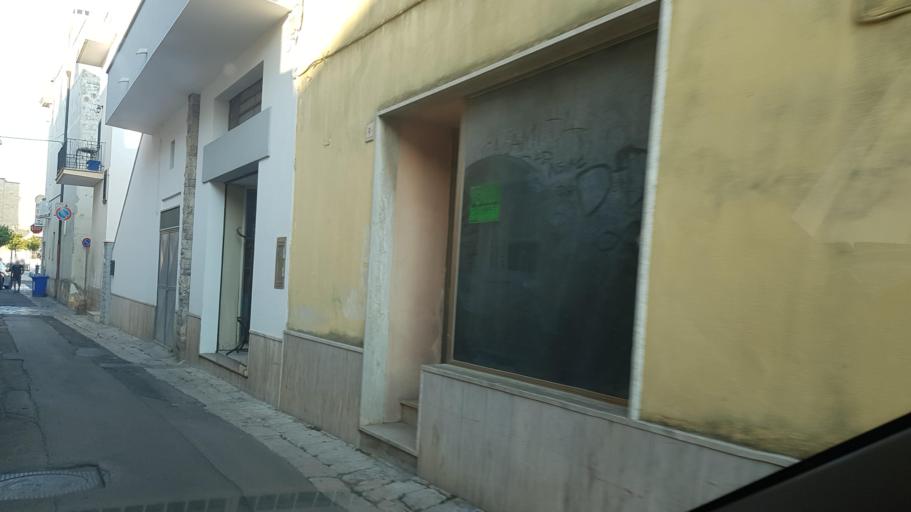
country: IT
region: Apulia
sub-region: Provincia di Lecce
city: Ruffano
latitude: 39.9835
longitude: 18.2473
